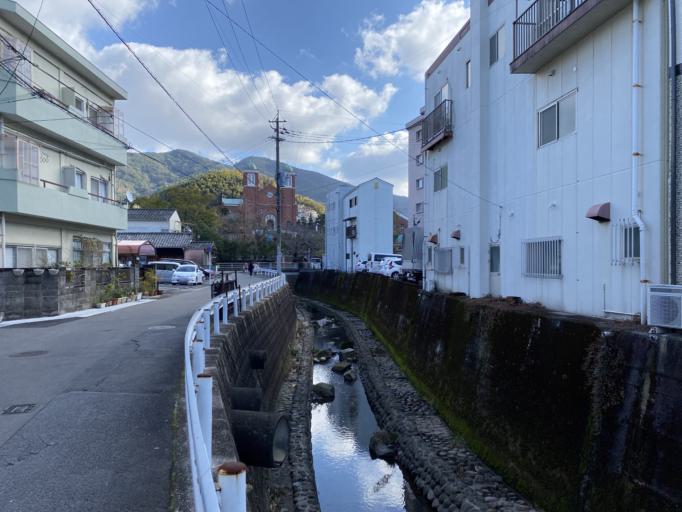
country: JP
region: Nagasaki
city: Nagasaki-shi
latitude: 32.7769
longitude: 129.8658
